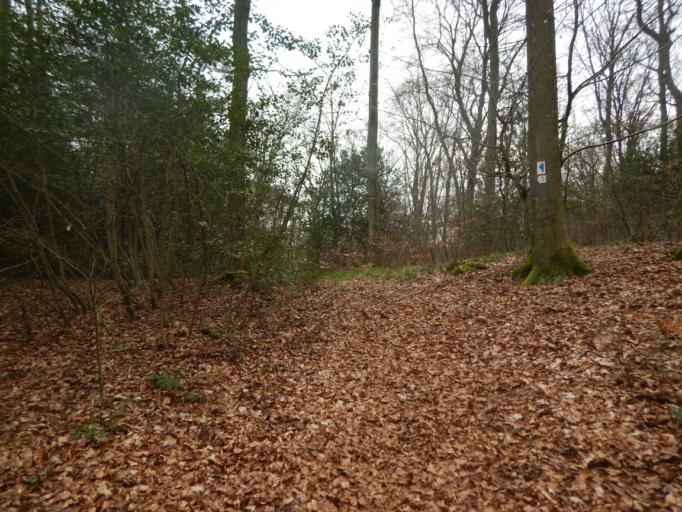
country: LU
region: Grevenmacher
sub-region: Canton d'Echternach
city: Beaufort
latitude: 49.8331
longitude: 6.3232
